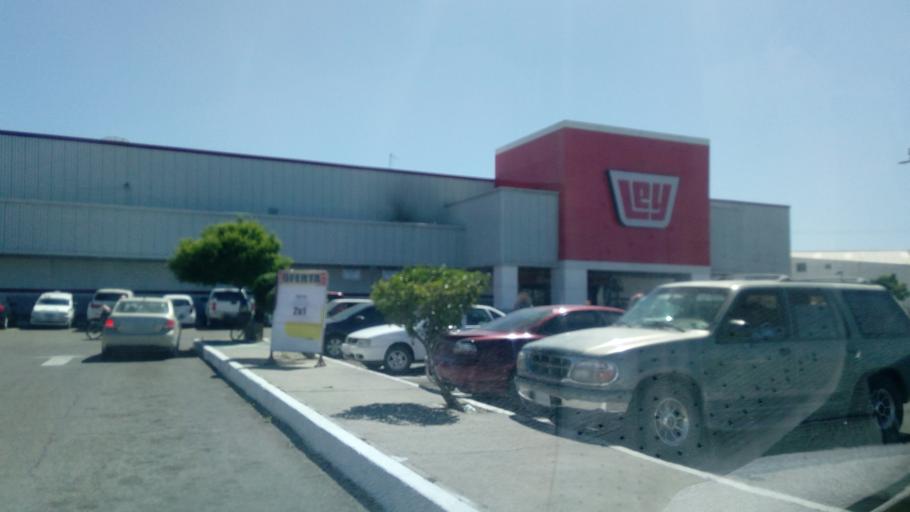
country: MX
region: Durango
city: Victoria de Durango
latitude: 24.0311
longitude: -104.6287
